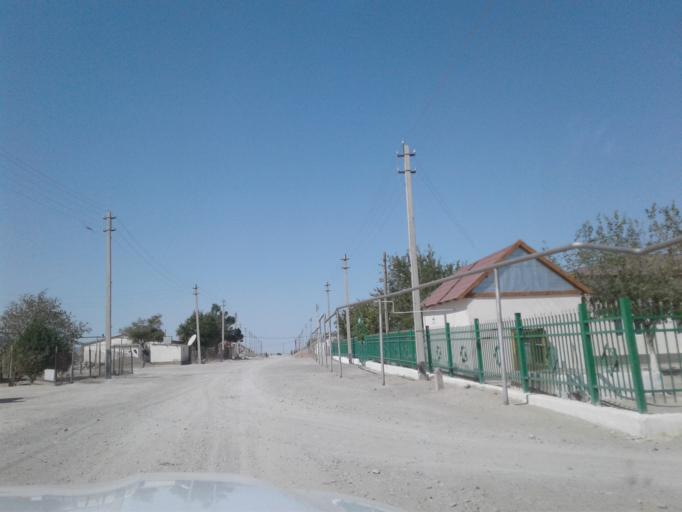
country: TM
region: Balkan
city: Gazanjyk
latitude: 39.1518
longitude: 55.3129
